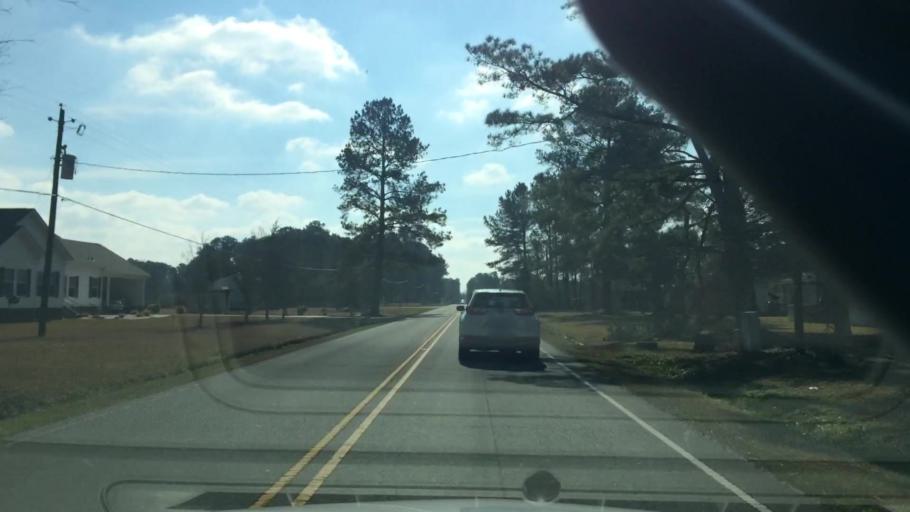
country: US
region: North Carolina
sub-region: Duplin County
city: Beulaville
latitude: 34.8745
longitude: -77.7908
